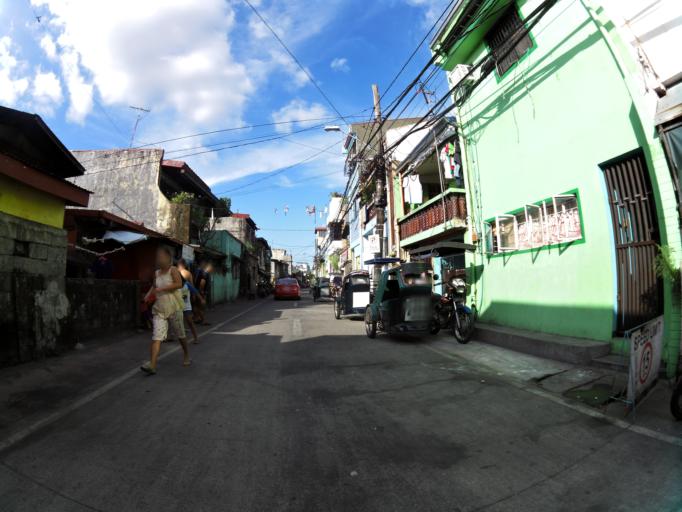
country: PH
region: Metro Manila
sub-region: Marikina
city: Calumpang
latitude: 14.6384
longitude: 121.0976
